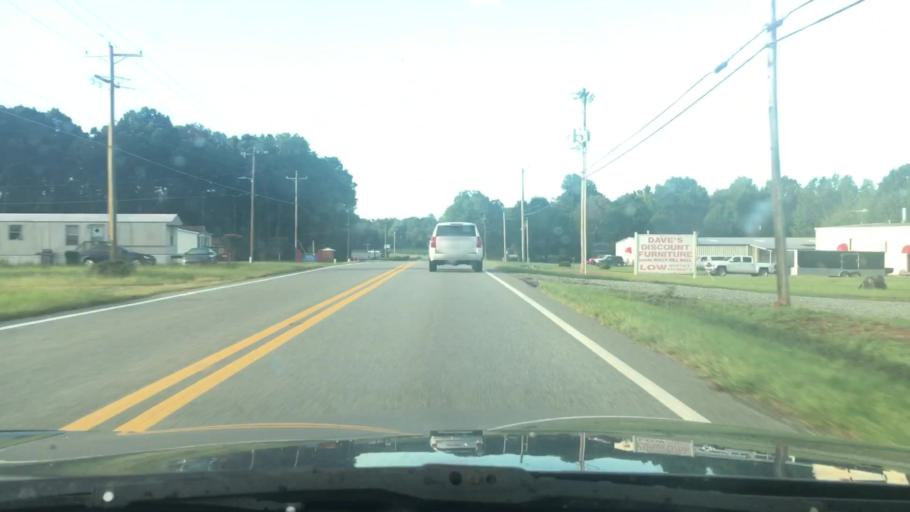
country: US
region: North Carolina
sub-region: Alamance County
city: Green Level
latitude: 36.1531
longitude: -79.3373
